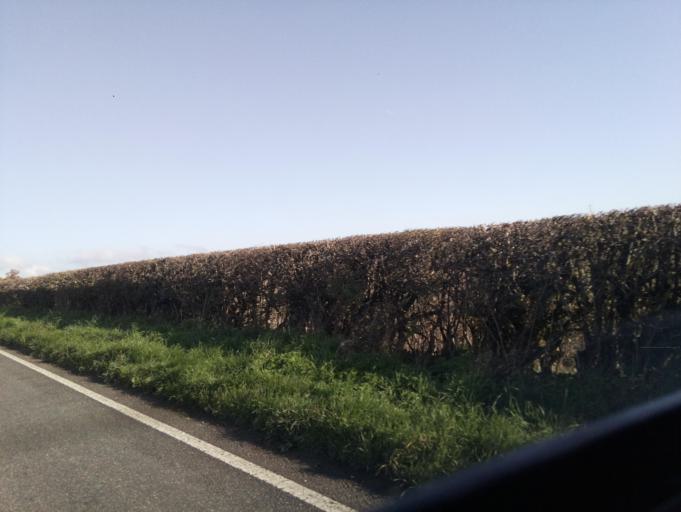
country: GB
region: England
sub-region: Somerset
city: Frome
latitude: 51.2017
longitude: -2.3193
